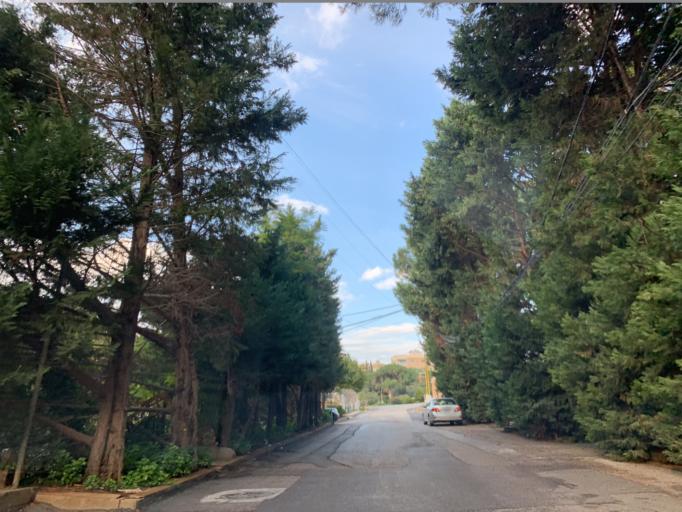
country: LB
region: Mont-Liban
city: Baabda
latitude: 33.8528
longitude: 35.5774
